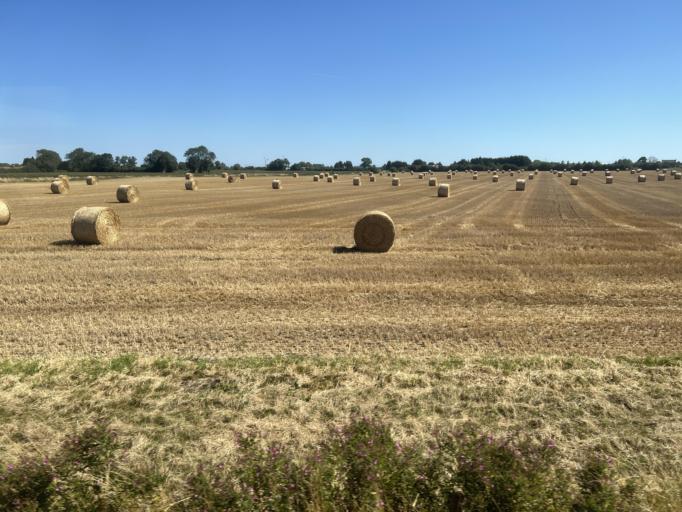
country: GB
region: England
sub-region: Lincolnshire
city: Wainfleet All Saints
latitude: 53.1292
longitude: 0.1944
